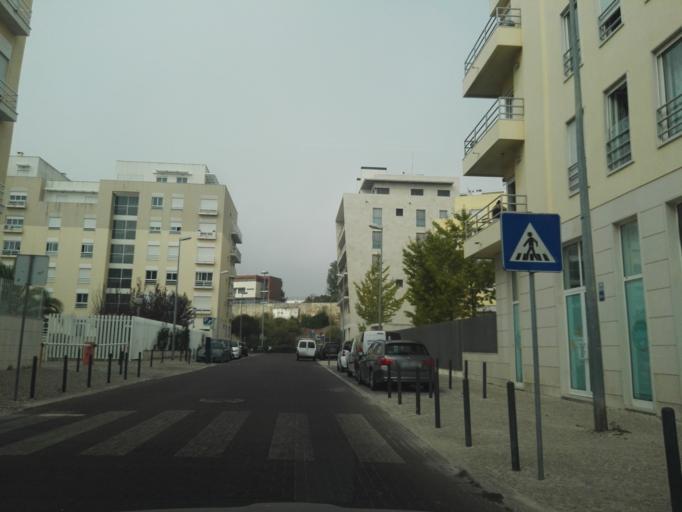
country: PT
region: Lisbon
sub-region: Loures
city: Moscavide
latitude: 38.7595
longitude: -9.0952
